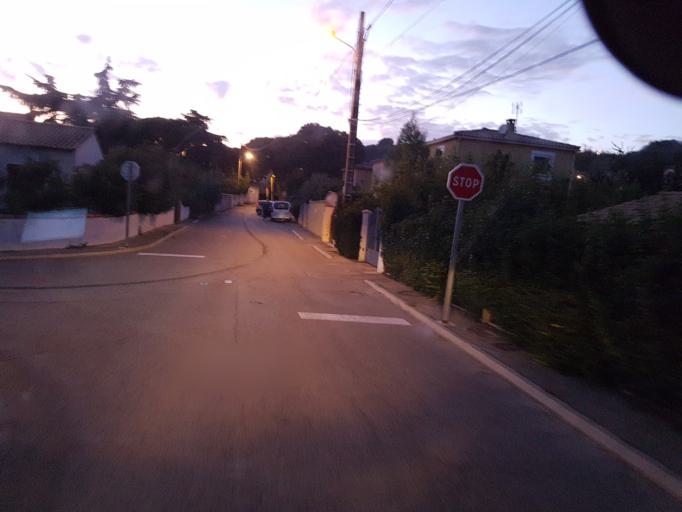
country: FR
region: Languedoc-Roussillon
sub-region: Departement du Gard
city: Bellegarde
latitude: 43.7502
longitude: 4.5123
